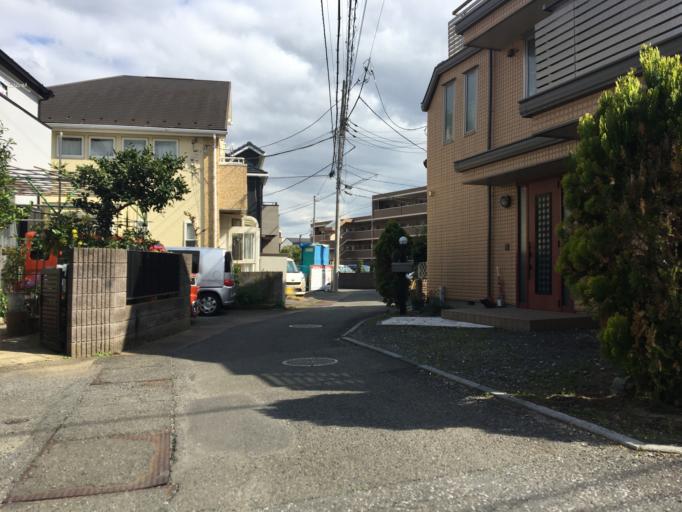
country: JP
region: Tokyo
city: Chofugaoka
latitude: 35.6473
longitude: 139.5069
